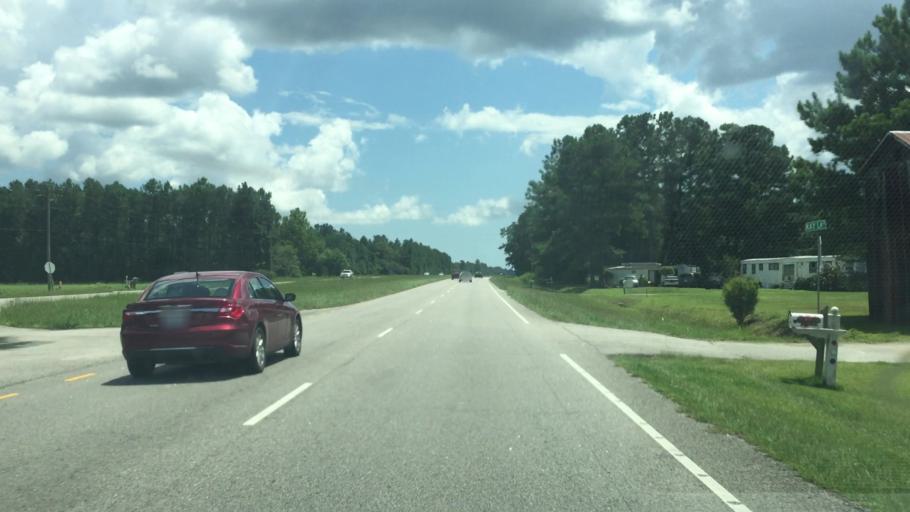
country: US
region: South Carolina
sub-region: Horry County
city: Loris
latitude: 33.9785
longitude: -78.7438
